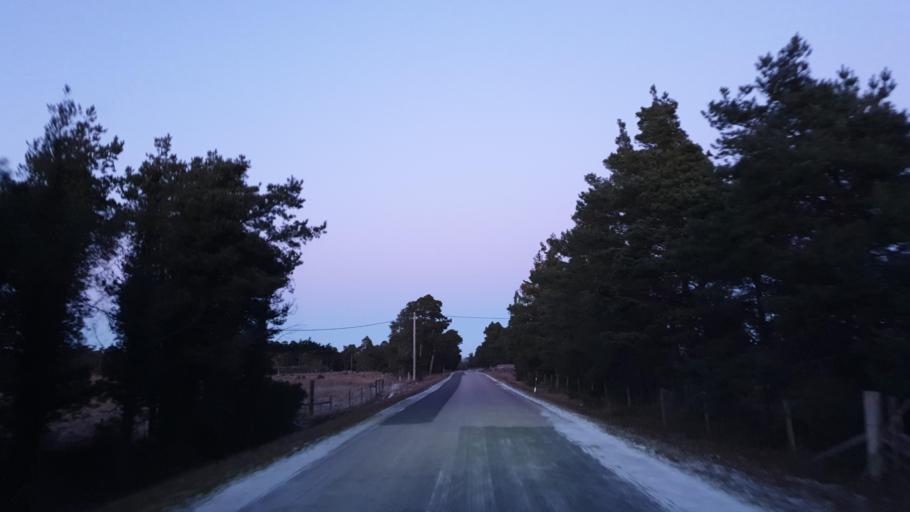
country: SE
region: Gotland
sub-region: Gotland
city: Slite
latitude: 57.4129
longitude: 18.8113
